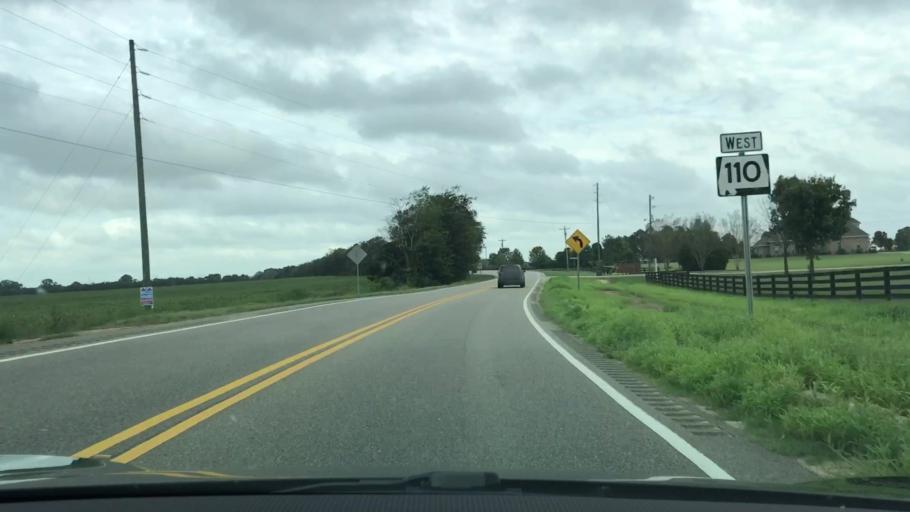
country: US
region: Alabama
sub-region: Montgomery County
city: Pike Road
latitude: 32.3157
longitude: -86.0473
